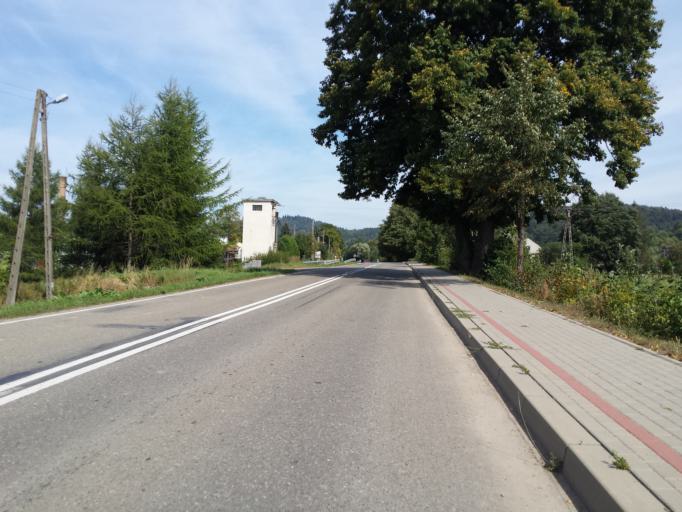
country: PL
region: Subcarpathian Voivodeship
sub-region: Powiat leski
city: Baligrod
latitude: 49.3428
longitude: 22.2900
